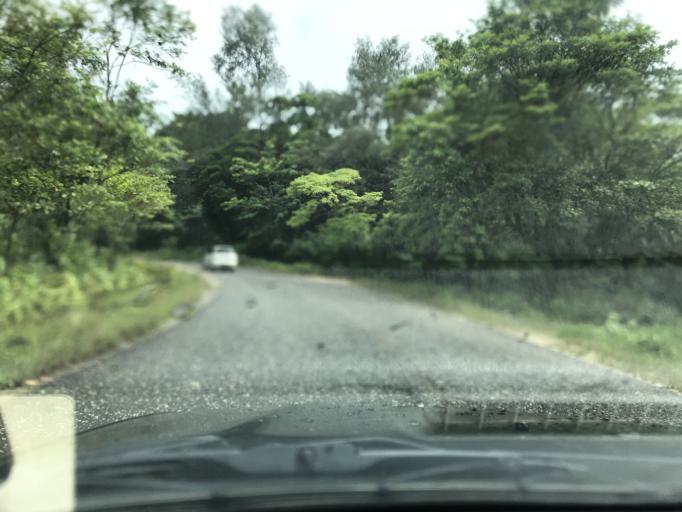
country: SB
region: Western Province
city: Gizo
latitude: -8.3235
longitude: 157.2571
